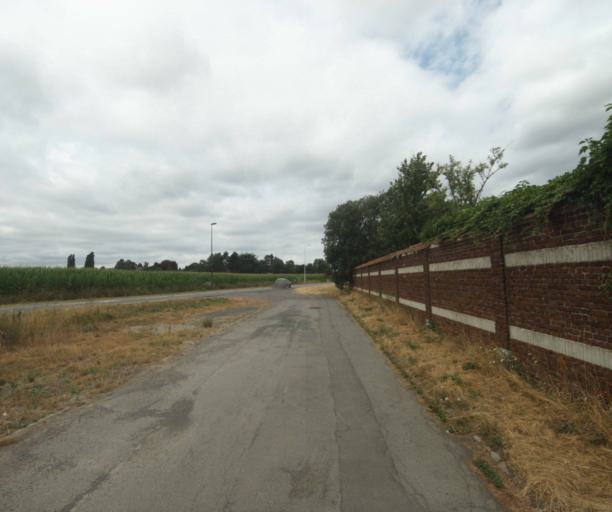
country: FR
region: Nord-Pas-de-Calais
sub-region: Departement du Nord
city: Roncq
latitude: 50.7447
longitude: 3.1088
